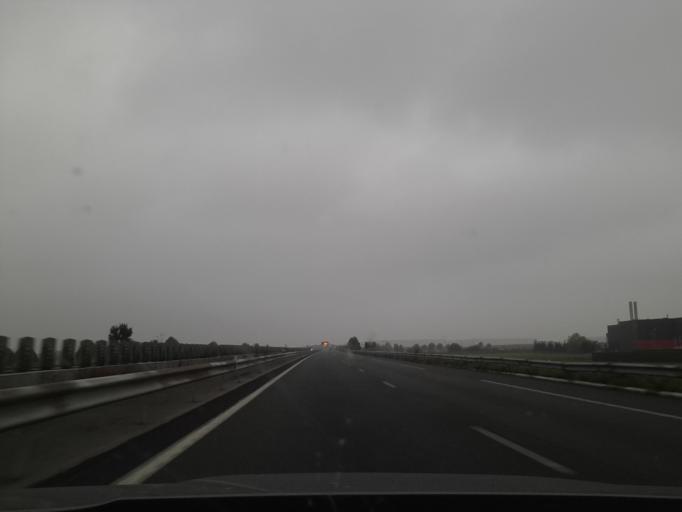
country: FR
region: Nord-Pas-de-Calais
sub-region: Departement du Nord
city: Neuville-Saint-Remy
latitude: 50.2010
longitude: 3.2164
